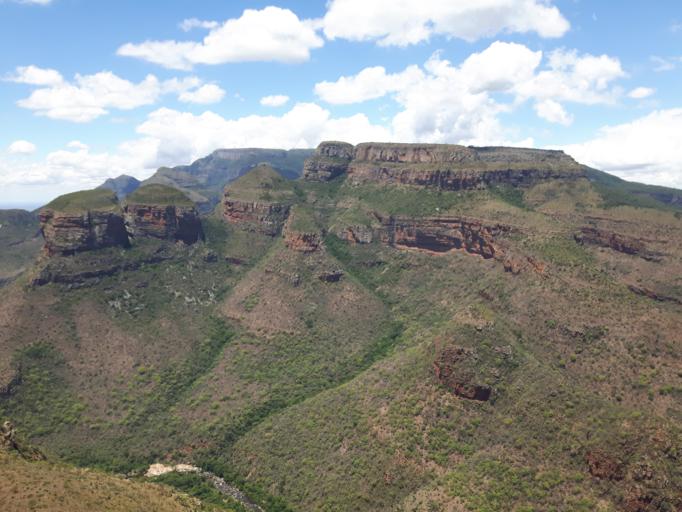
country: ZA
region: Limpopo
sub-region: Mopani District Municipality
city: Hoedspruit
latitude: -24.5737
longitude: 30.7990
